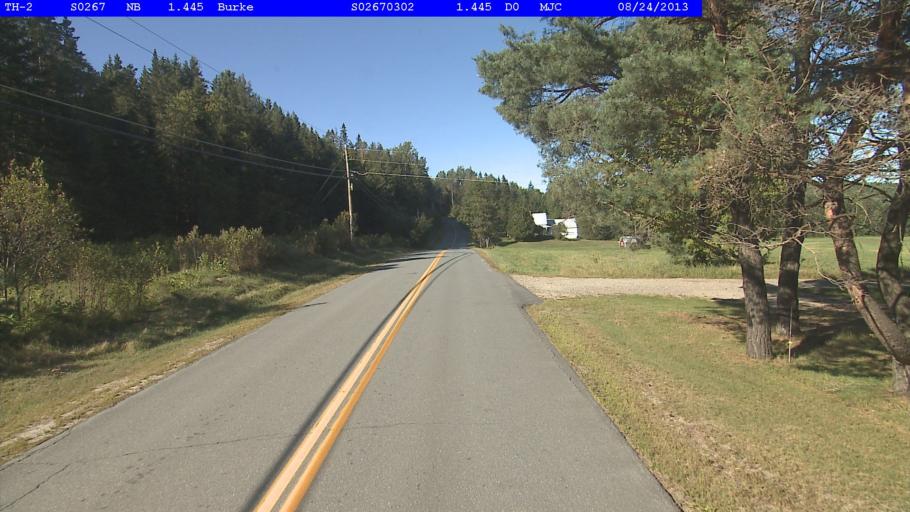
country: US
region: Vermont
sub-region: Caledonia County
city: Lyndonville
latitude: 44.6069
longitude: -71.9374
